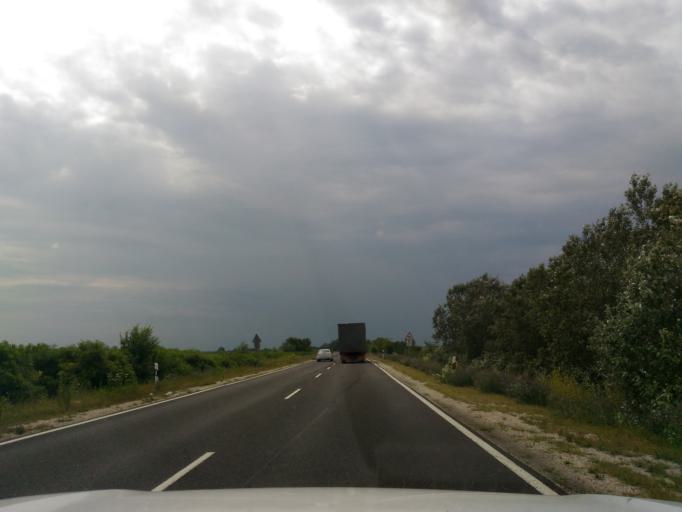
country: HU
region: Pest
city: Abony
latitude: 47.2022
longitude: 20.0757
